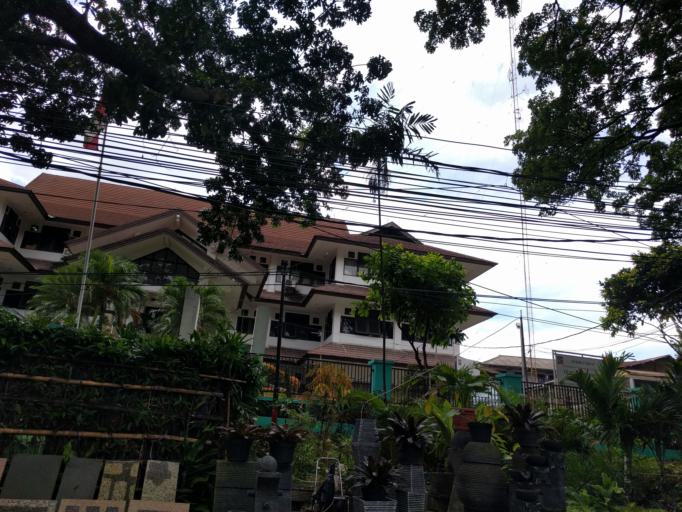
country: ID
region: West Java
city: Bogor
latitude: -6.5732
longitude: 106.8083
